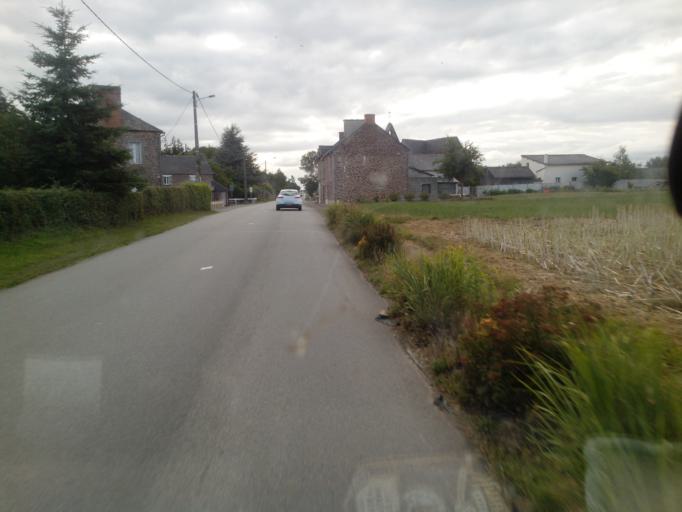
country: FR
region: Brittany
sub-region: Departement du Morbihan
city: Mauron
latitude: 48.0743
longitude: -2.2490
